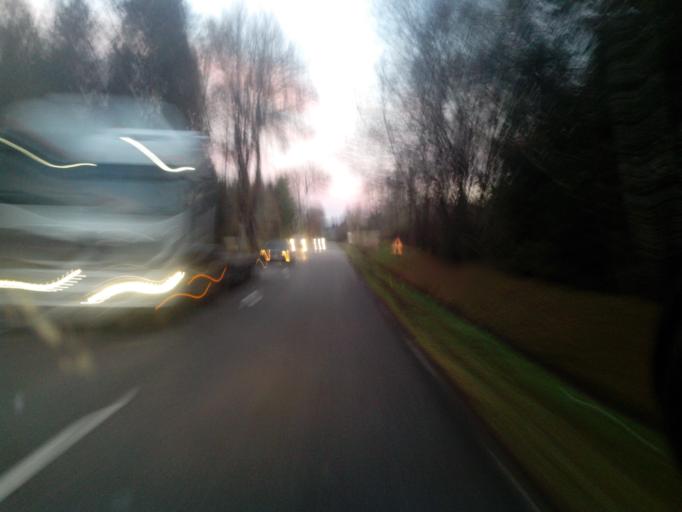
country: FR
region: Limousin
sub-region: Departement de la Correze
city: Meymac
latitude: 45.5060
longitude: 2.2085
